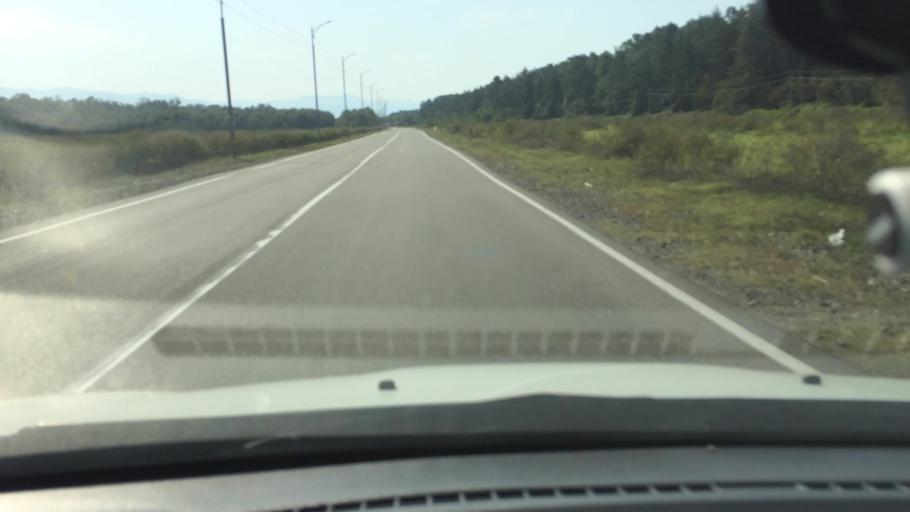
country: GE
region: Guria
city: Urek'i
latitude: 41.9511
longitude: 41.7704
